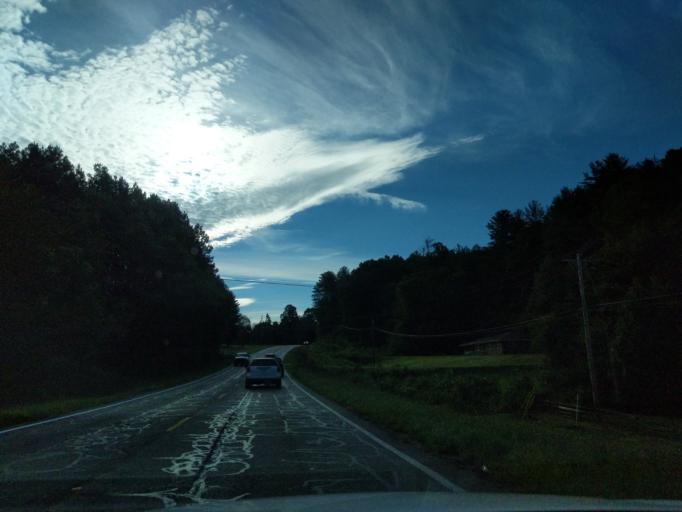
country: US
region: Georgia
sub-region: Fannin County
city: Blue Ridge
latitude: 34.8859
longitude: -84.3366
